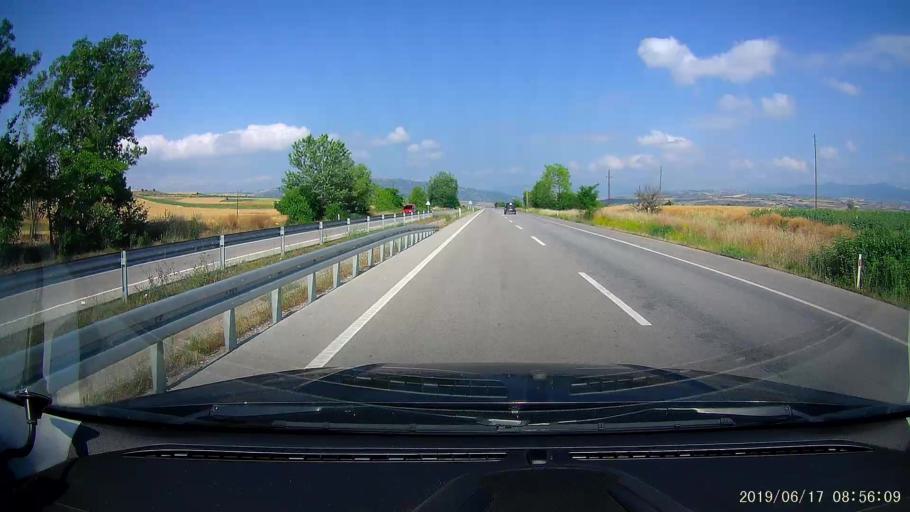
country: TR
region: Amasya
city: Esencay
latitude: 40.7333
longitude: 36.4285
